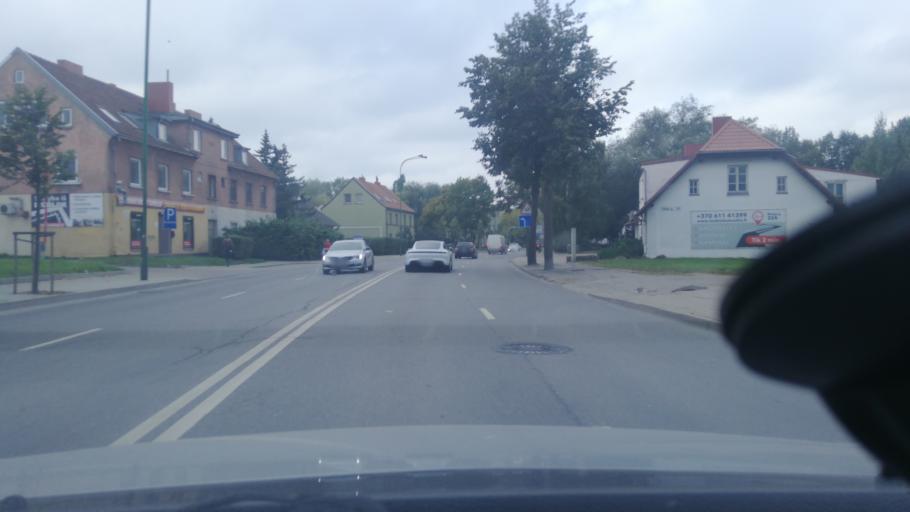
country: LT
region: Klaipedos apskritis
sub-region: Klaipeda
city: Klaipeda
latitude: 55.7044
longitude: 21.1549
